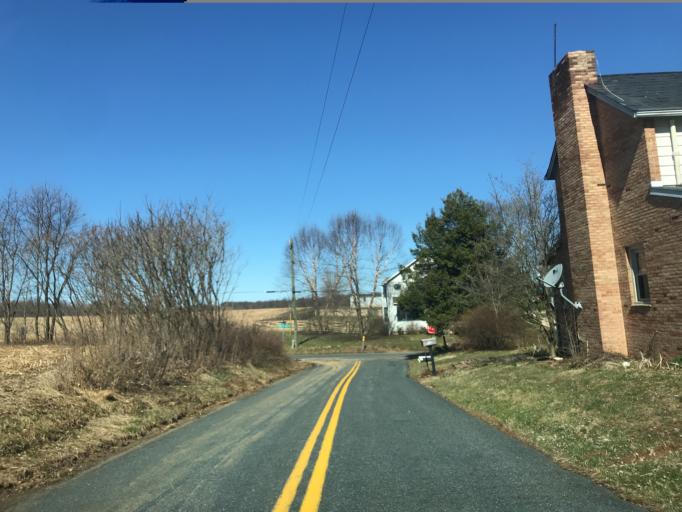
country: US
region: Pennsylvania
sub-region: York County
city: Stewartstown
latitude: 39.7119
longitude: -76.5267
